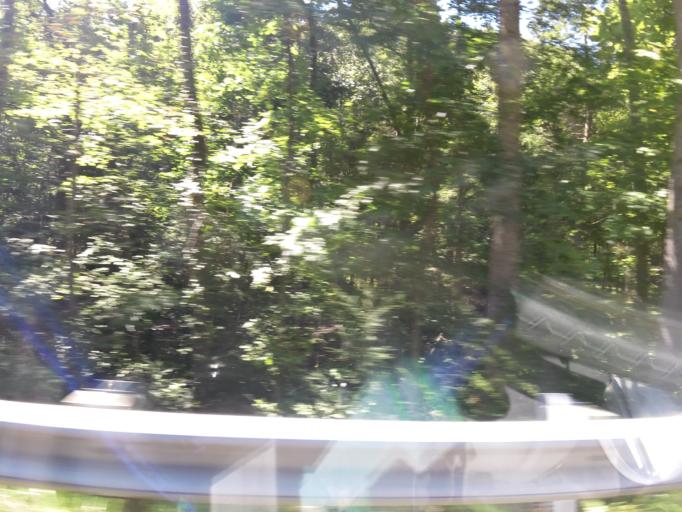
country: US
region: Kentucky
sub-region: Leslie County
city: Hyden
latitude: 37.1311
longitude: -83.4617
